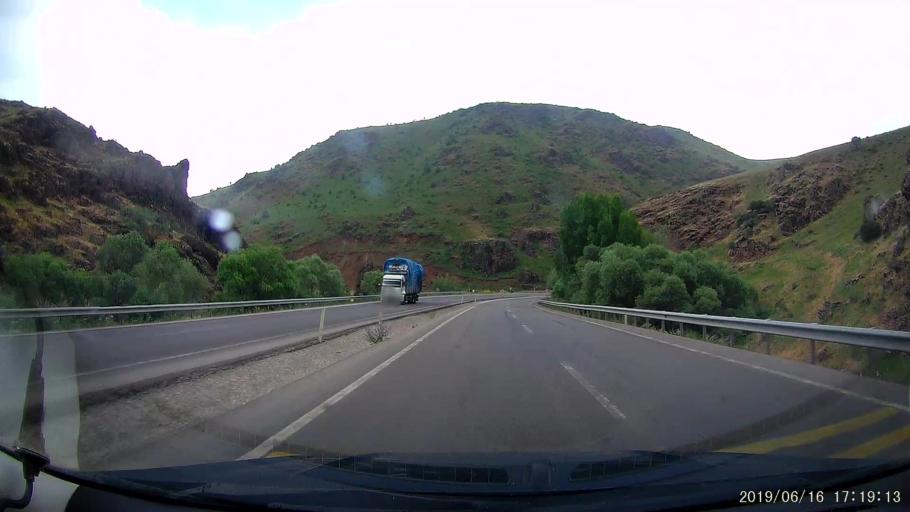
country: TR
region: Erzincan
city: Tercan
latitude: 39.8028
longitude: 40.5310
